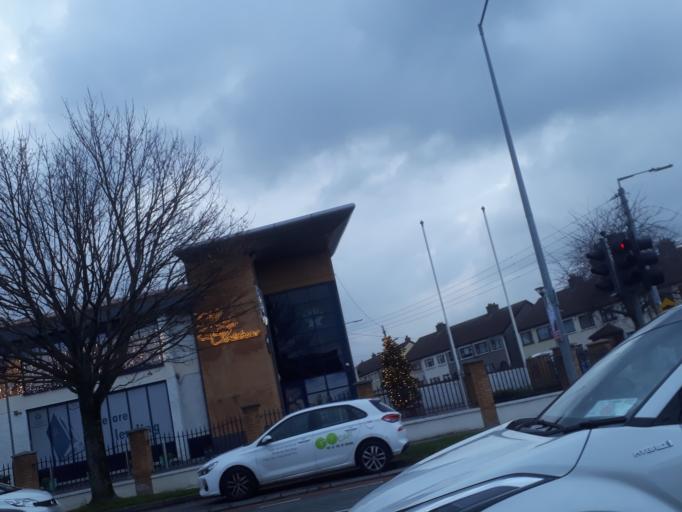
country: IE
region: Leinster
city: Crumlin
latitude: 53.3139
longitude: -6.3294
